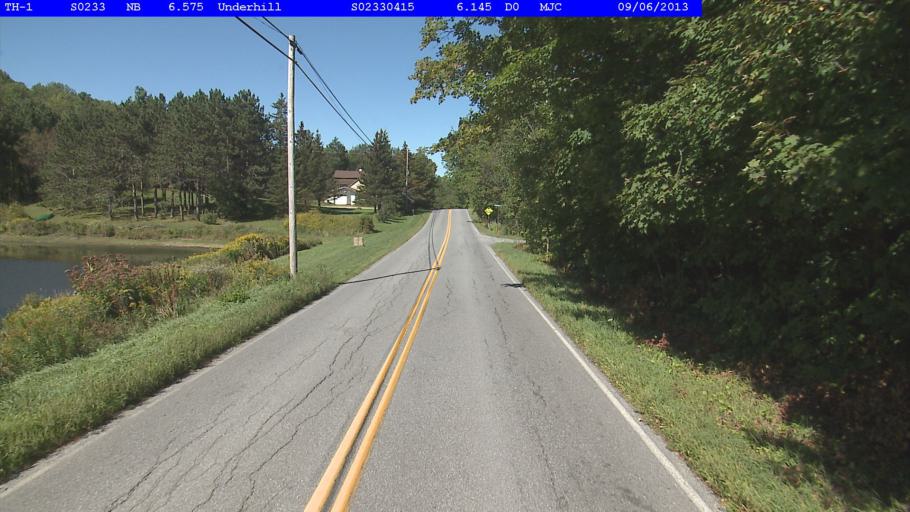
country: US
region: Vermont
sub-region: Chittenden County
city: Jericho
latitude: 44.5535
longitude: -72.8672
